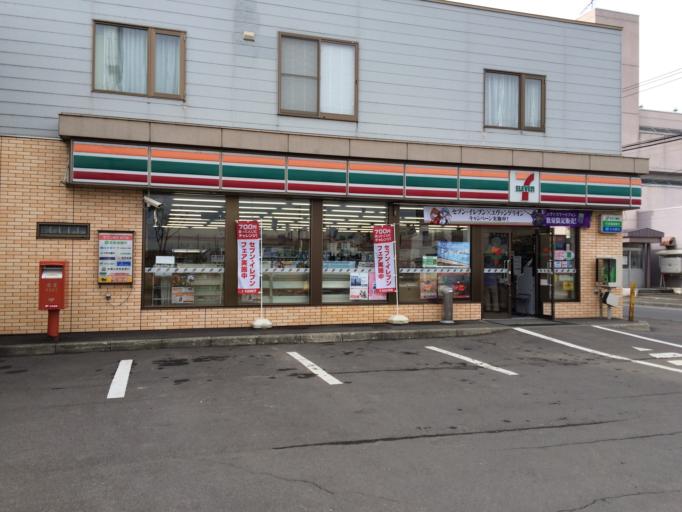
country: JP
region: Hokkaido
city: Iwamizawa
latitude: 43.2039
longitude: 141.7525
